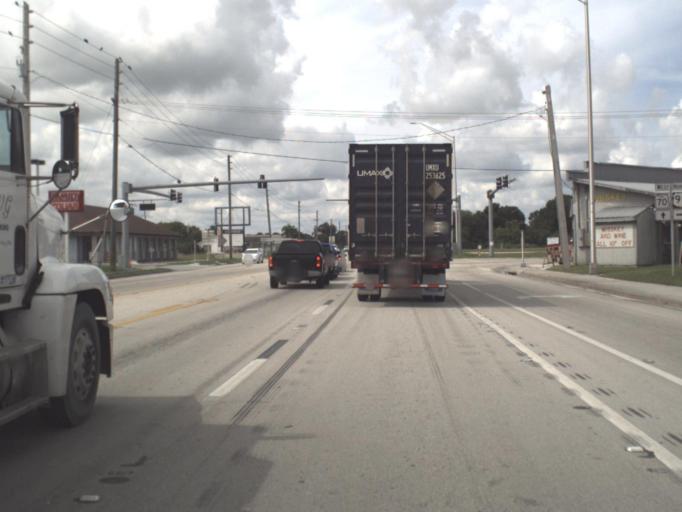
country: US
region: Florida
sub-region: Okeechobee County
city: Okeechobee
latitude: 27.2436
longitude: -80.8481
